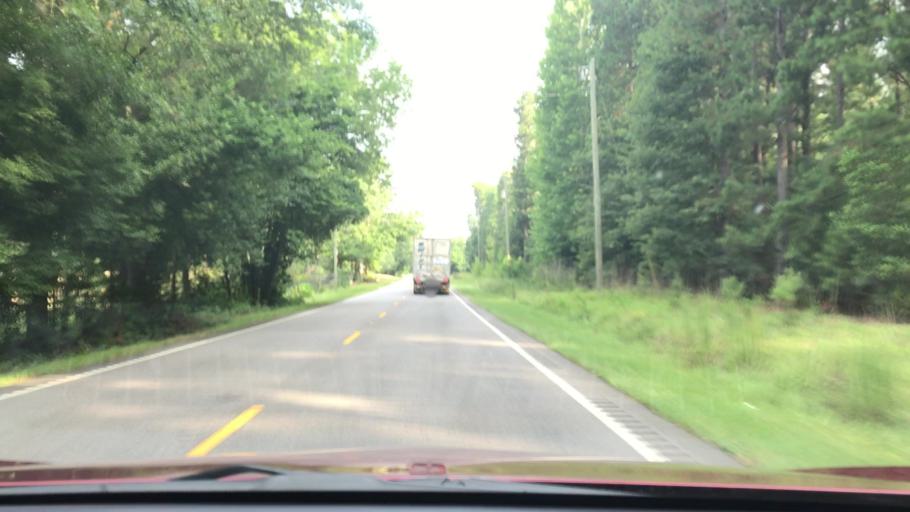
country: US
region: South Carolina
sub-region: Barnwell County
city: Williston
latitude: 33.6175
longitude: -81.2870
